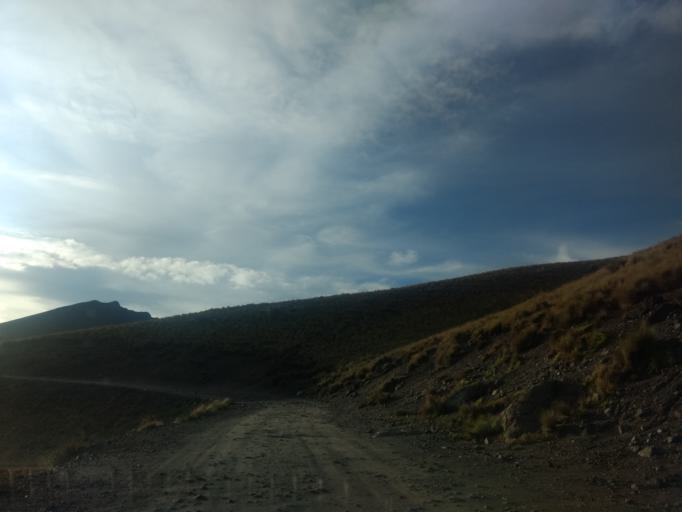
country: MX
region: Mexico
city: Cerro La Calera
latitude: 19.1200
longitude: -99.7527
